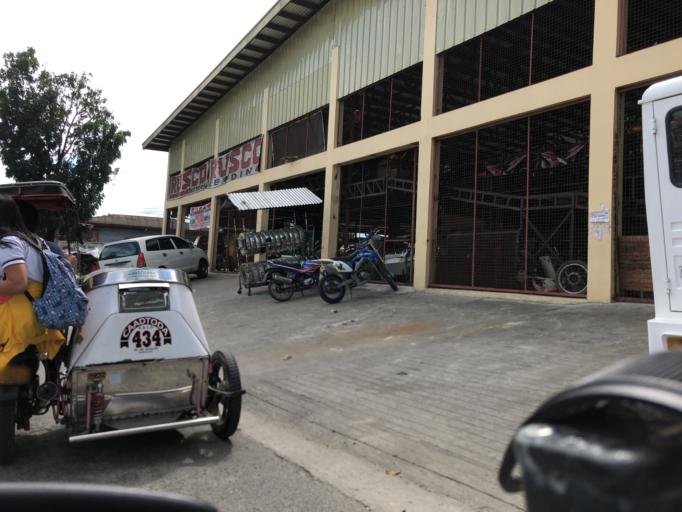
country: PH
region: Central Luzon
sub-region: Province of Bulacan
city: San Jose del Monte
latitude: 14.7573
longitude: 121.0553
